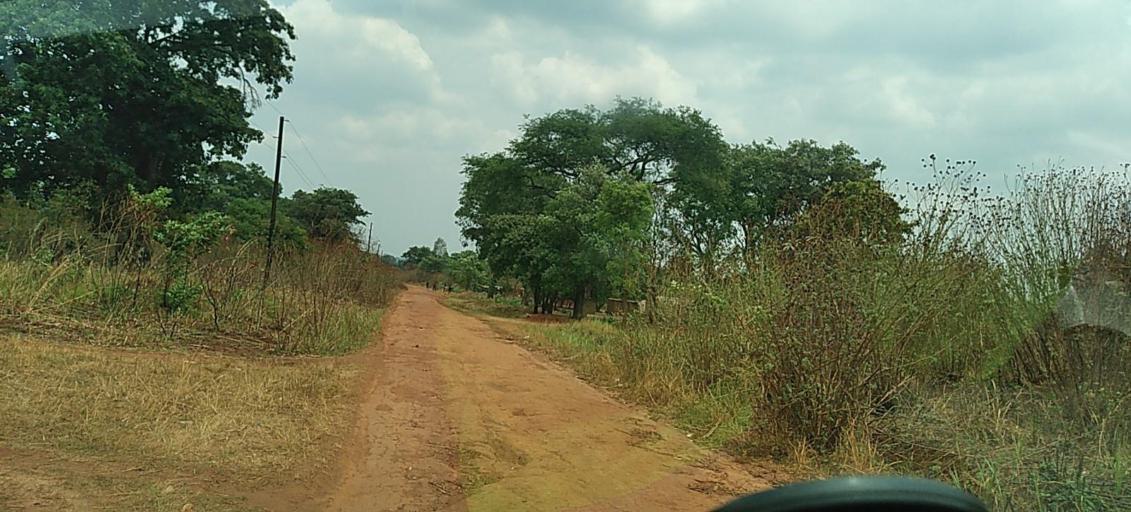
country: ZM
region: North-Western
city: Kansanshi
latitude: -12.0387
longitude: 26.3993
